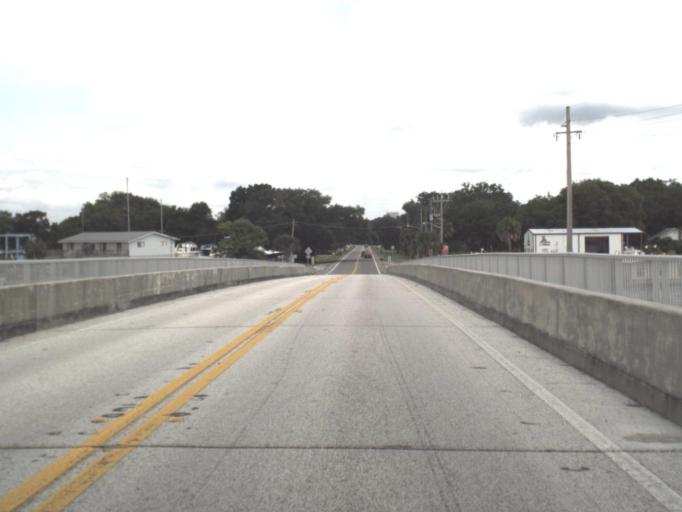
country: US
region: Florida
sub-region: Duval County
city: Atlantic Beach
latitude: 30.4054
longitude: -81.5086
